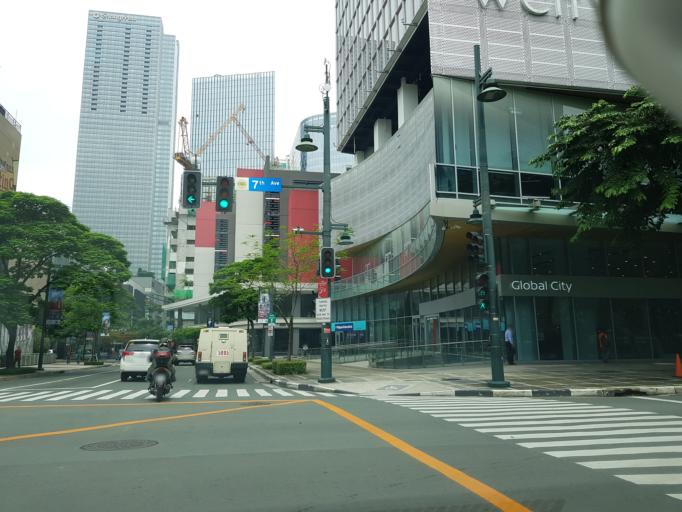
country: PH
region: Metro Manila
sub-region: Makati City
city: Makati City
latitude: 14.5522
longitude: 121.0500
